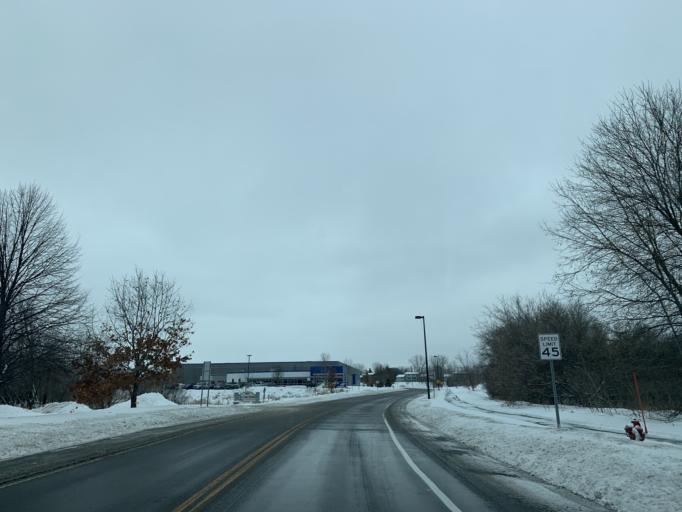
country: US
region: Minnesota
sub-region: Ramsey County
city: North Saint Paul
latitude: 45.0248
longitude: -92.9698
